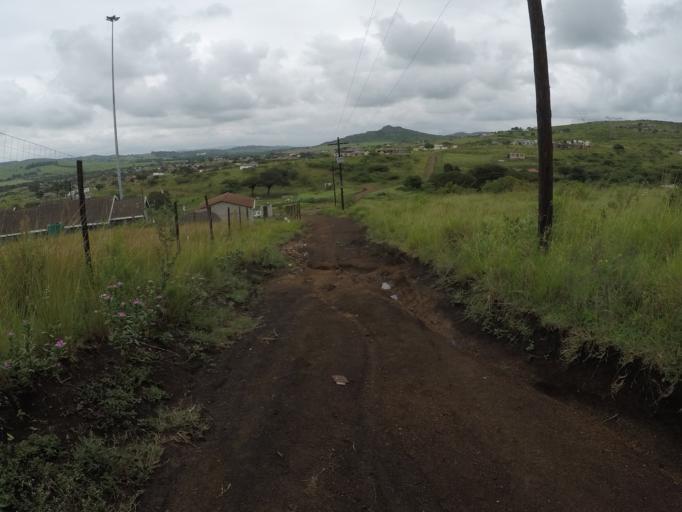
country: ZA
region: KwaZulu-Natal
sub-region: uThungulu District Municipality
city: Empangeni
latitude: -28.7091
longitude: 31.8500
